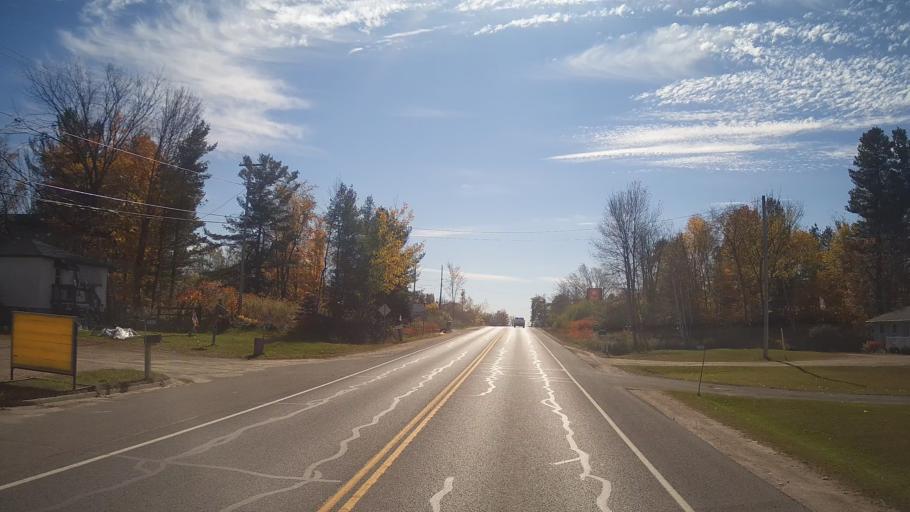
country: CA
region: Ontario
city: Perth
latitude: 44.7893
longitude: -76.6778
